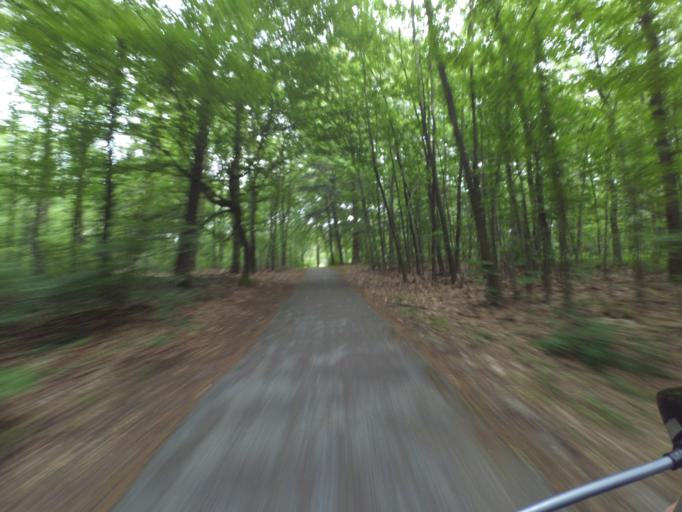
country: NL
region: Gelderland
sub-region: Gemeente Renkum
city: Wolfheze
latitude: 52.0007
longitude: 5.7988
